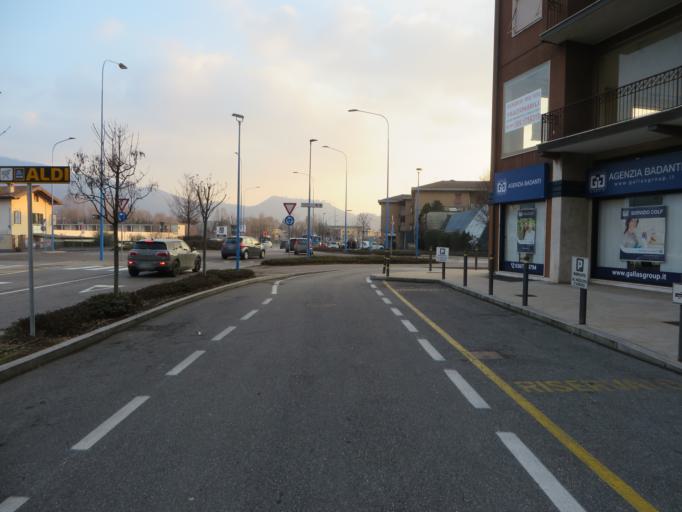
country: IT
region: Lombardy
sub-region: Provincia di Brescia
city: Bovezzo
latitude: 45.5733
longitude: 10.2312
